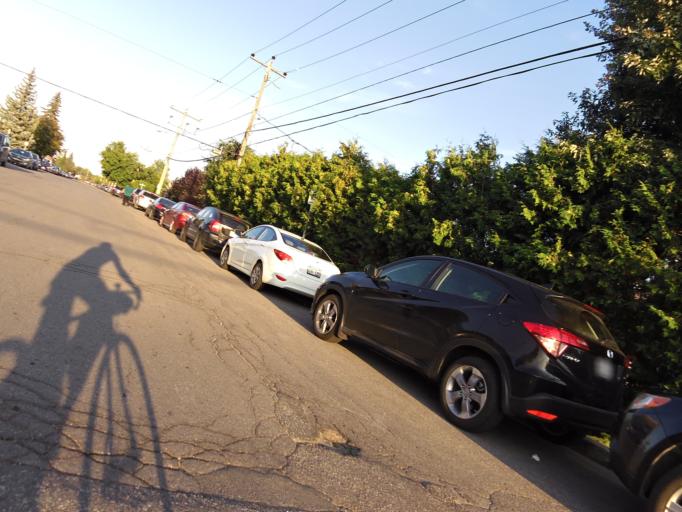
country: CA
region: Quebec
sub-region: Outaouais
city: Gatineau
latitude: 45.4654
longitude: -75.6991
